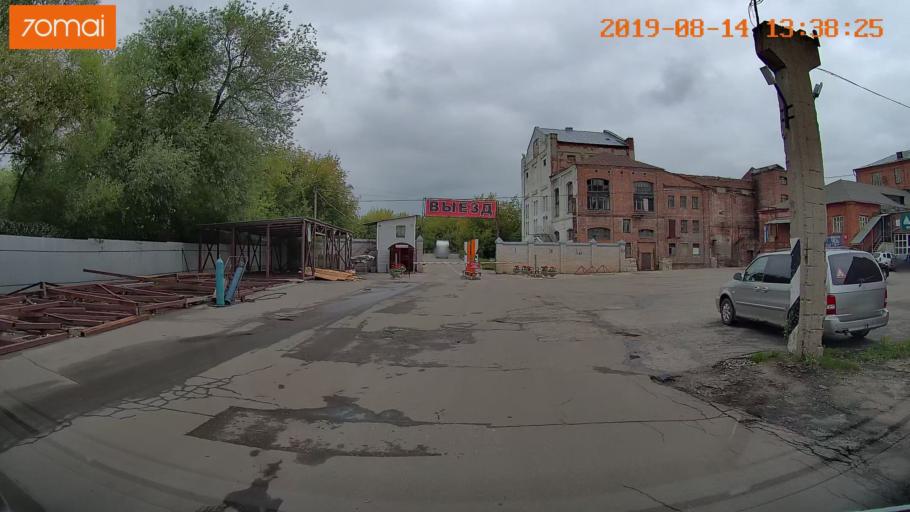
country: RU
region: Ivanovo
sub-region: Gorod Ivanovo
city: Ivanovo
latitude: 57.0093
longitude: 40.9650
